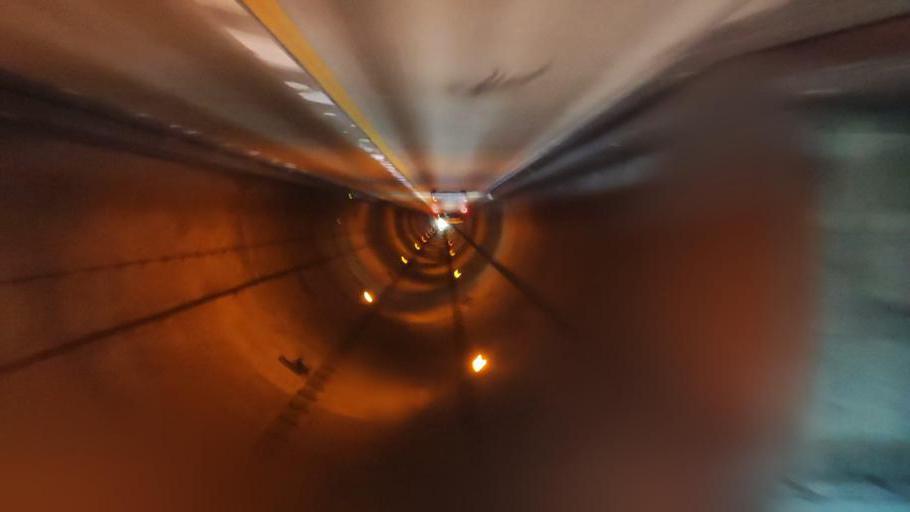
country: JP
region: Nara
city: Yoshino-cho
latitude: 34.2567
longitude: 136.0000
